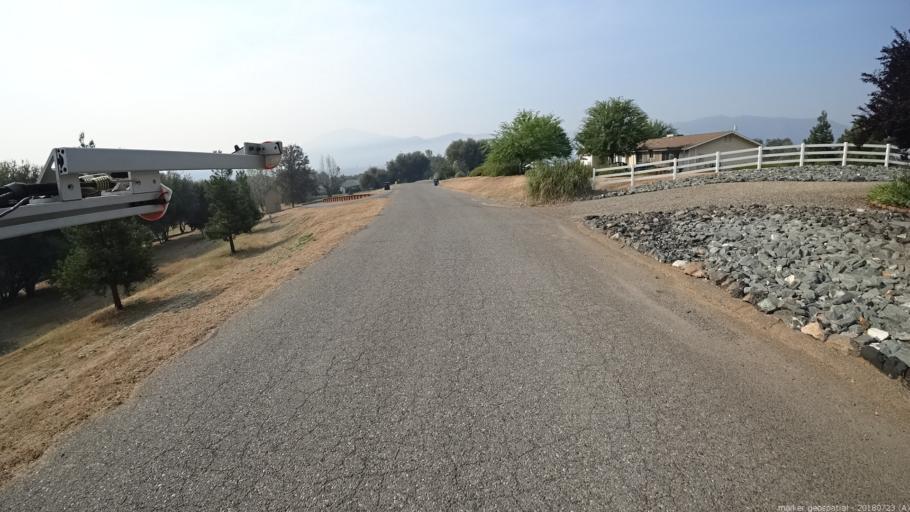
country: US
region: California
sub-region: Madera County
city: Ahwahnee
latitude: 37.3611
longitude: -119.7195
